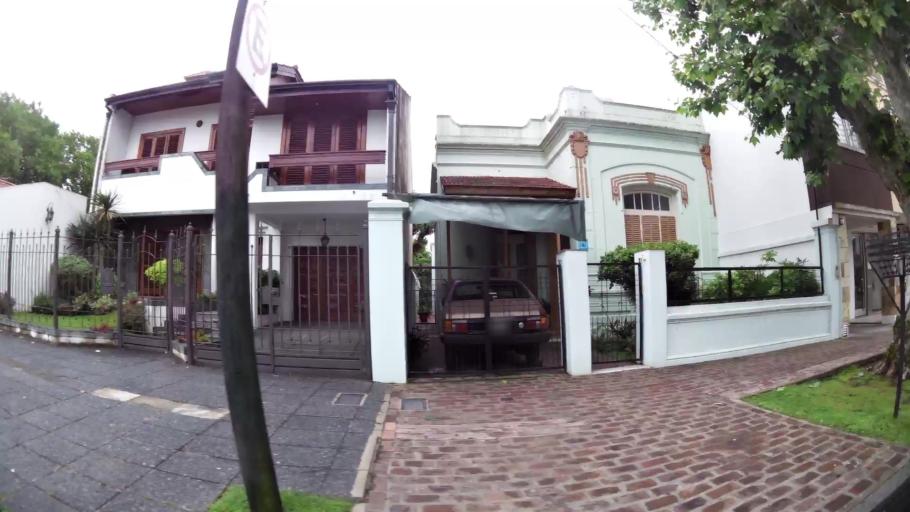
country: AR
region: Buenos Aires
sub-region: Partido de Lomas de Zamora
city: Lomas de Zamora
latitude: -34.7630
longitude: -58.3920
